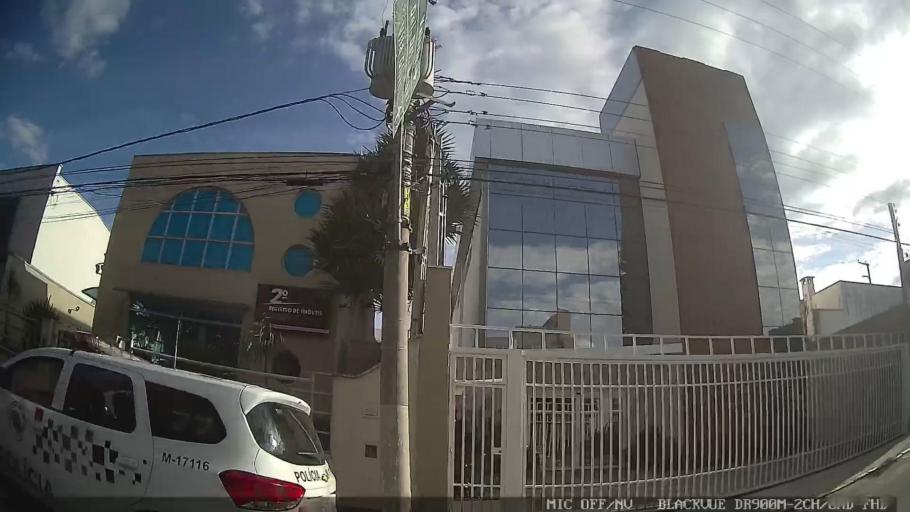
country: BR
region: Sao Paulo
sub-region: Mogi das Cruzes
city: Mogi das Cruzes
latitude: -23.5216
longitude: -46.1815
